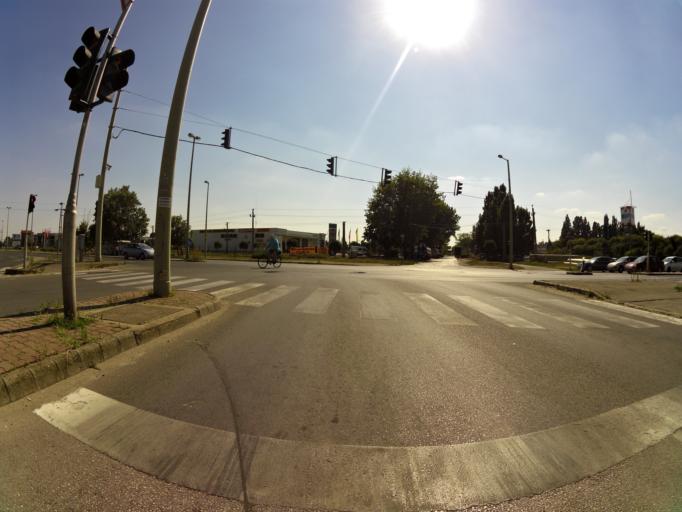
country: HU
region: Csongrad
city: Szeged
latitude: 46.2724
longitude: 20.1022
